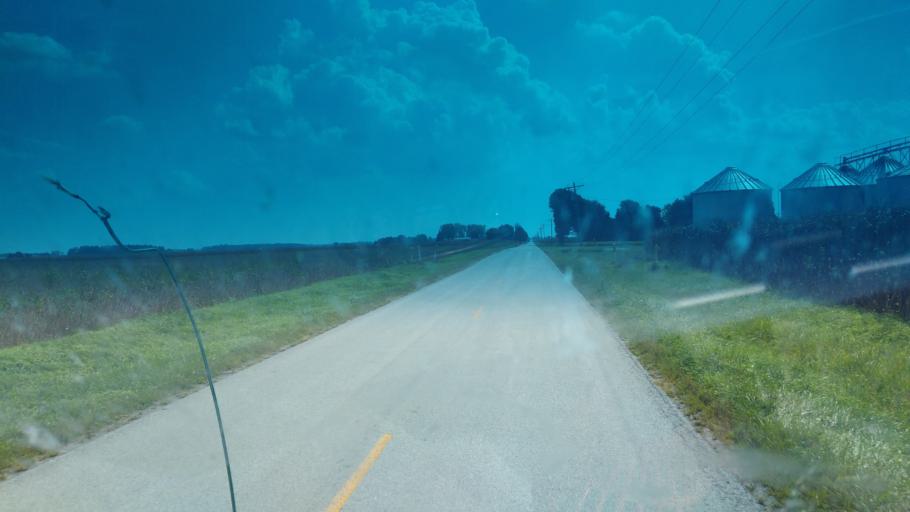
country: US
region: Ohio
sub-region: Hardin County
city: Kenton
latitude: 40.6666
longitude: -83.7276
